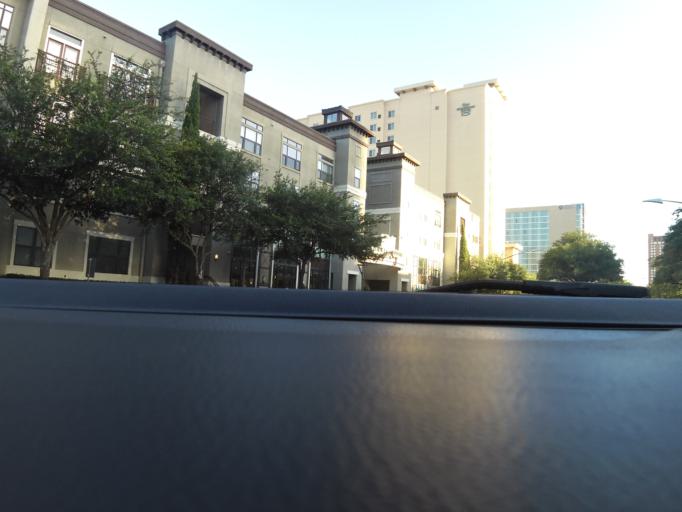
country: US
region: Texas
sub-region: Harris County
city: Bellaire
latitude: 29.7360
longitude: -95.4667
